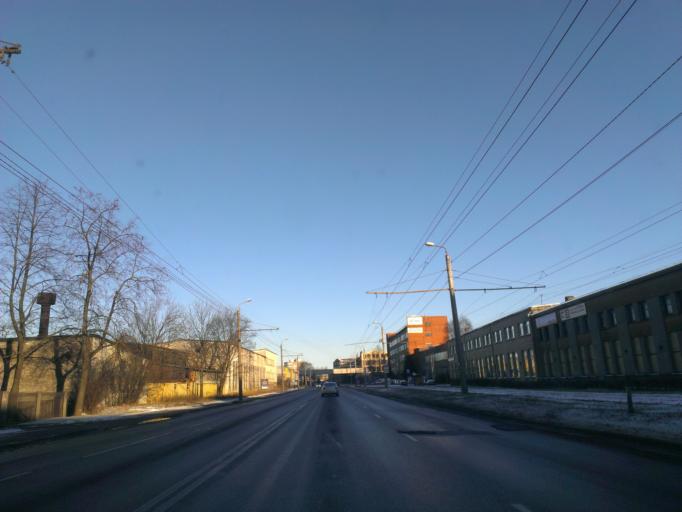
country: LV
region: Riga
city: Riga
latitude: 56.9824
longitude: 24.1181
